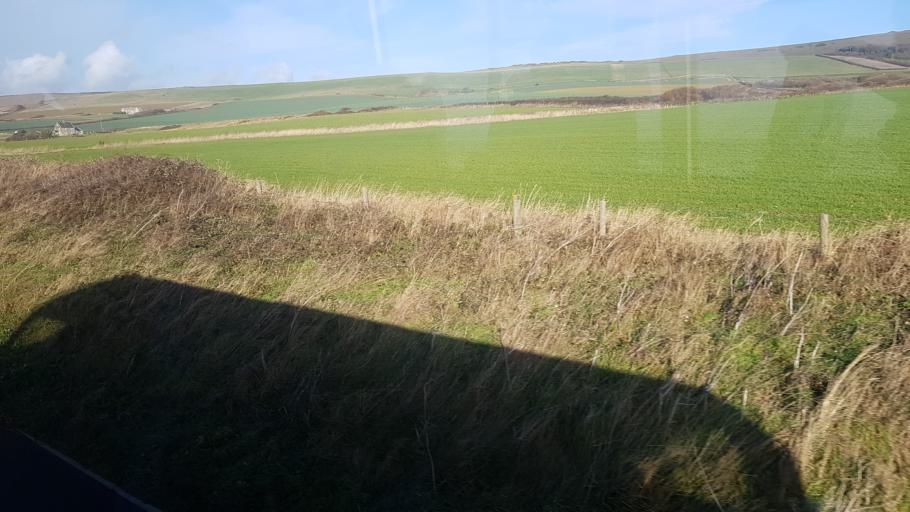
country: GB
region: England
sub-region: Isle of Wight
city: Freshwater
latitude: 50.6516
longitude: -1.4593
